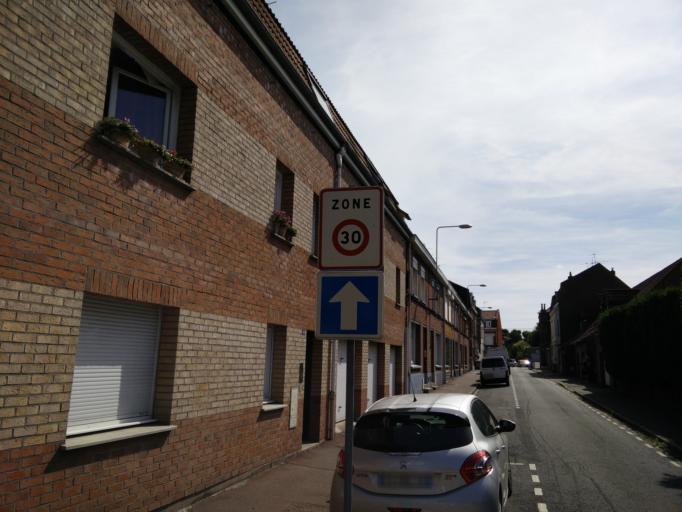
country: FR
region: Nord-Pas-de-Calais
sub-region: Departement du Nord
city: Marquette-lez-Lille
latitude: 50.6733
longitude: 3.0649
